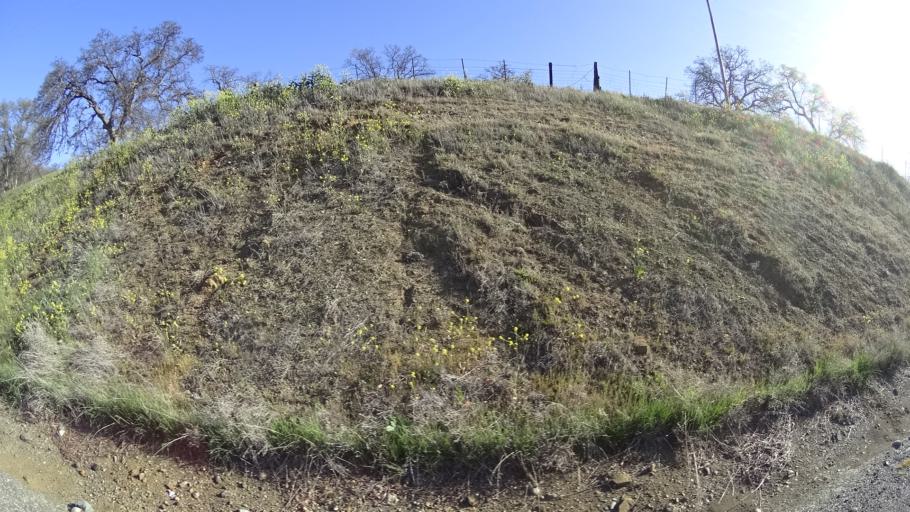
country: US
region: California
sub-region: Tehama County
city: Rancho Tehama Reserve
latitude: 39.7902
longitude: -122.5028
